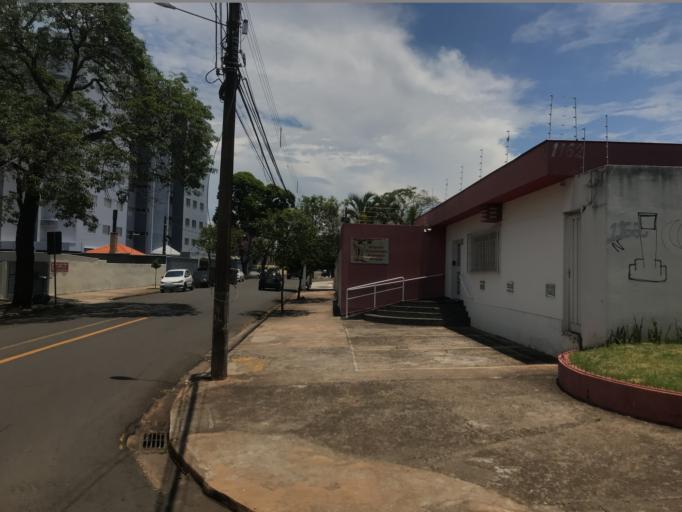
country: BR
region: Parana
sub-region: Londrina
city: Londrina
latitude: -23.3271
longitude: -51.1553
